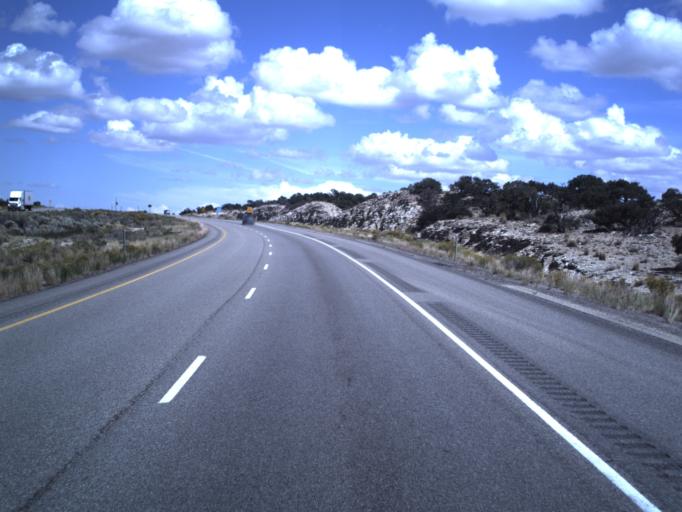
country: US
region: Utah
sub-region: Emery County
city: Ferron
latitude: 38.8480
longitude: -110.9318
